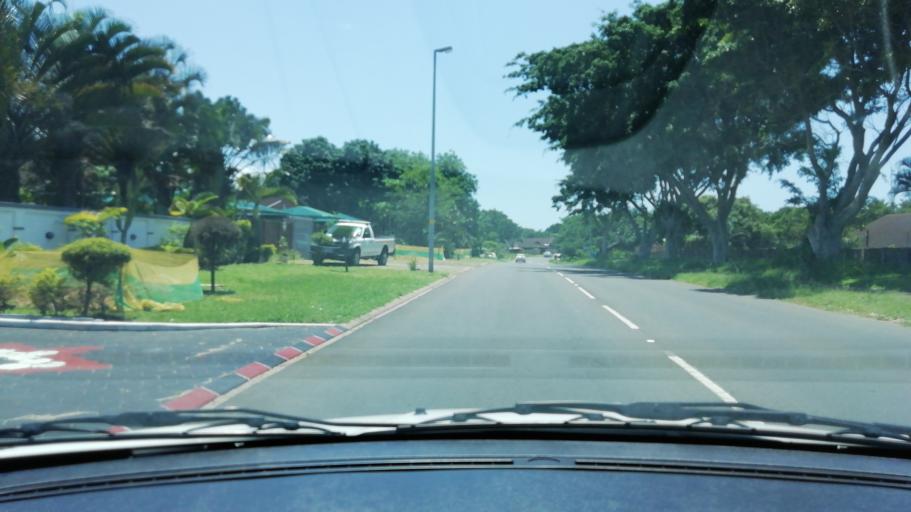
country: ZA
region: KwaZulu-Natal
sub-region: uThungulu District Municipality
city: Richards Bay
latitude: -28.7352
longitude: 32.0599
